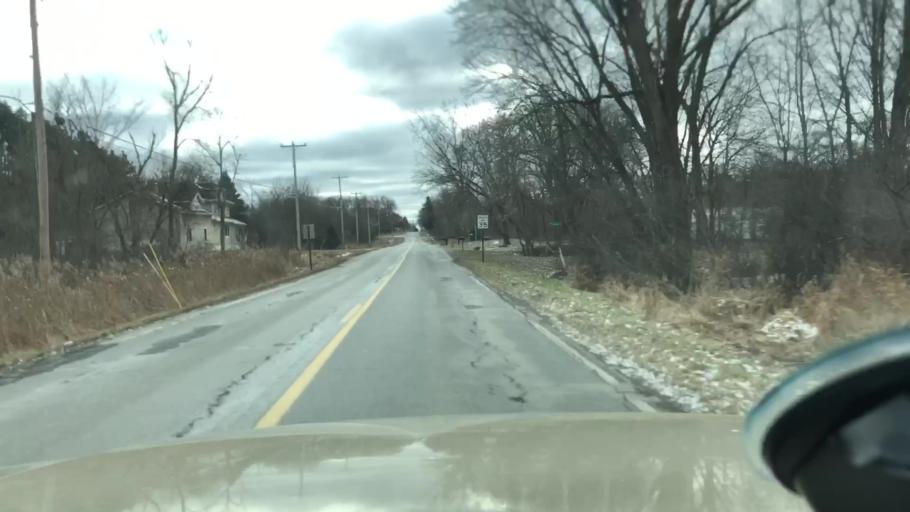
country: US
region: Michigan
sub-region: Jackson County
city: Jackson
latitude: 42.2657
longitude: -84.3649
